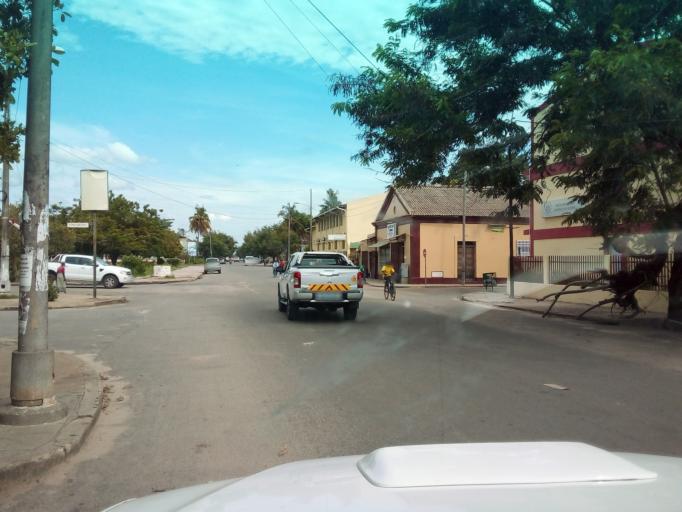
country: MZ
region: Zambezia
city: Quelimane
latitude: -17.8800
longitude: 36.8866
